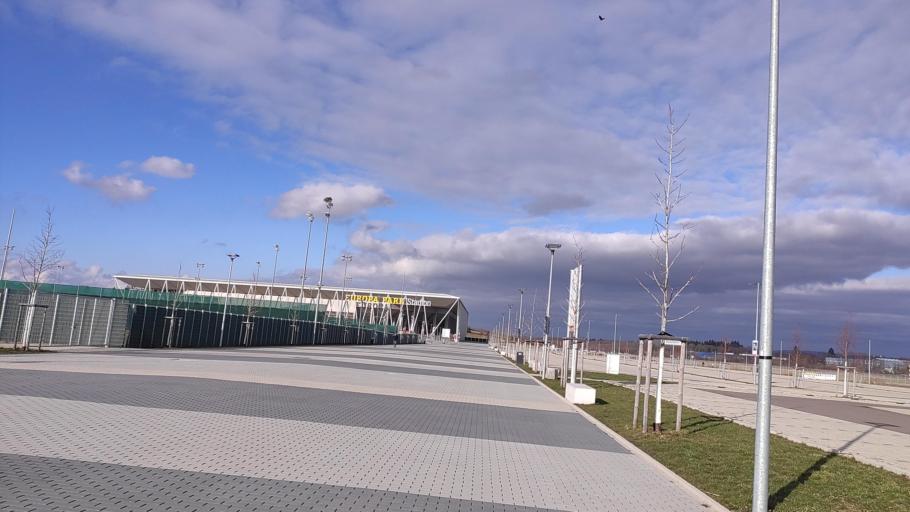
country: DE
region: Baden-Wuerttemberg
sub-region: Freiburg Region
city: Freiburg
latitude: 48.0185
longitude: 7.8327
